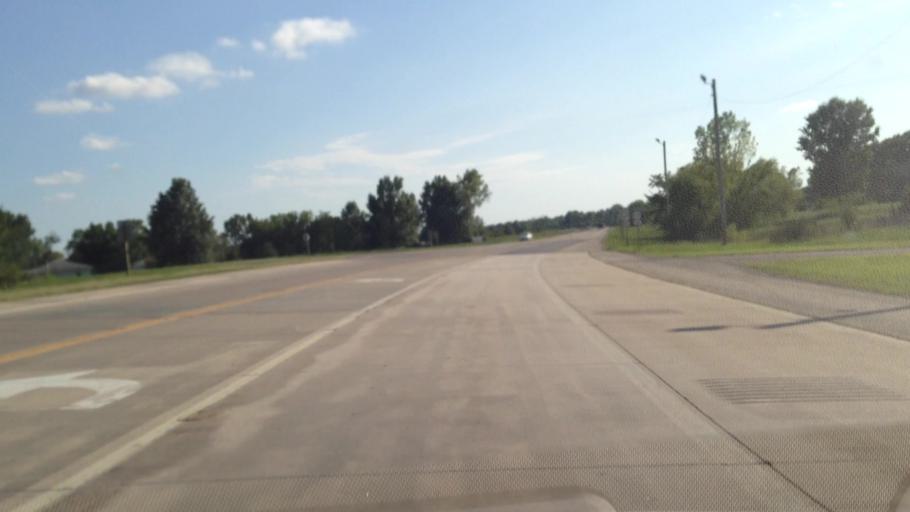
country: US
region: Kansas
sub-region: Crawford County
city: Arma
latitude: 37.5557
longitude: -94.7054
